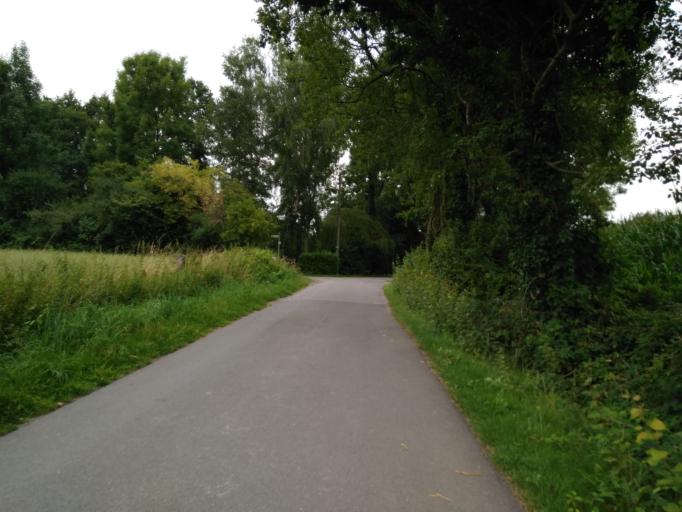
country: DE
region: North Rhine-Westphalia
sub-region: Regierungsbezirk Munster
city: Bottrop
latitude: 51.5951
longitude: 6.9075
